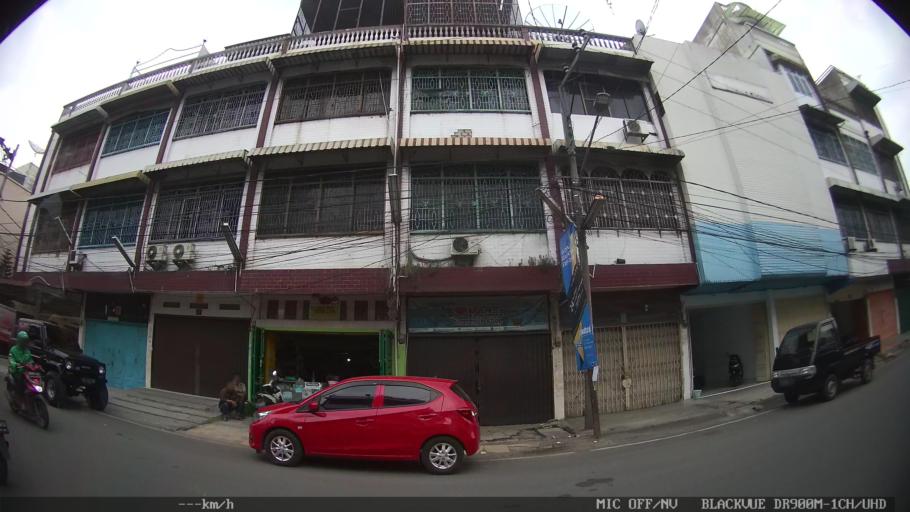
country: ID
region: North Sumatra
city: Medan
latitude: 3.5861
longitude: 98.7002
